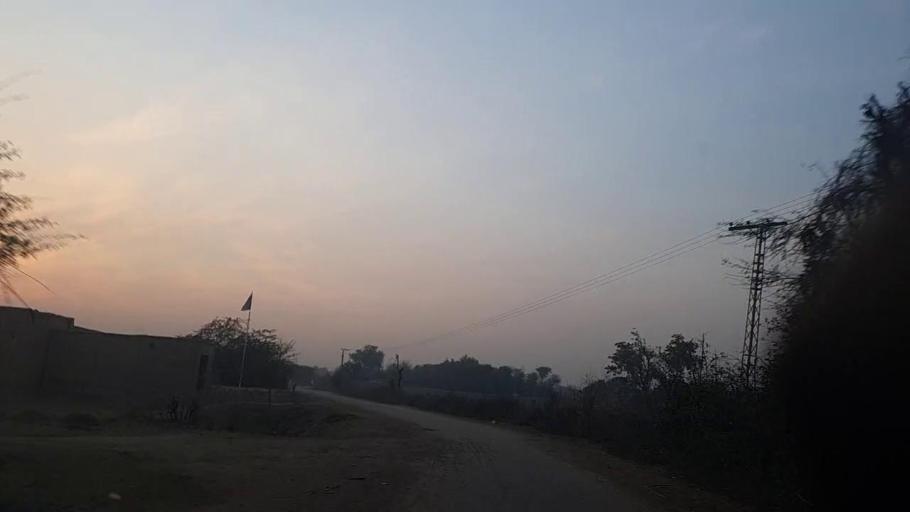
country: PK
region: Sindh
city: Sakrand
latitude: 26.1009
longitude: 68.3193
